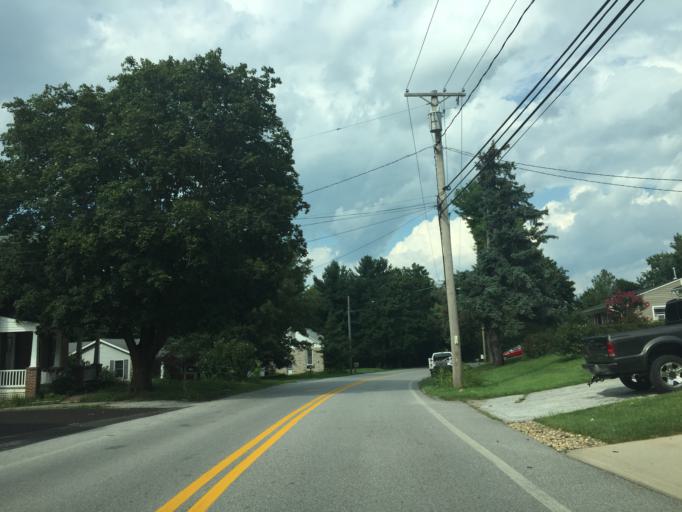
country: US
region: Maryland
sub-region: Carroll County
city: Westminster
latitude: 39.5906
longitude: -76.9938
